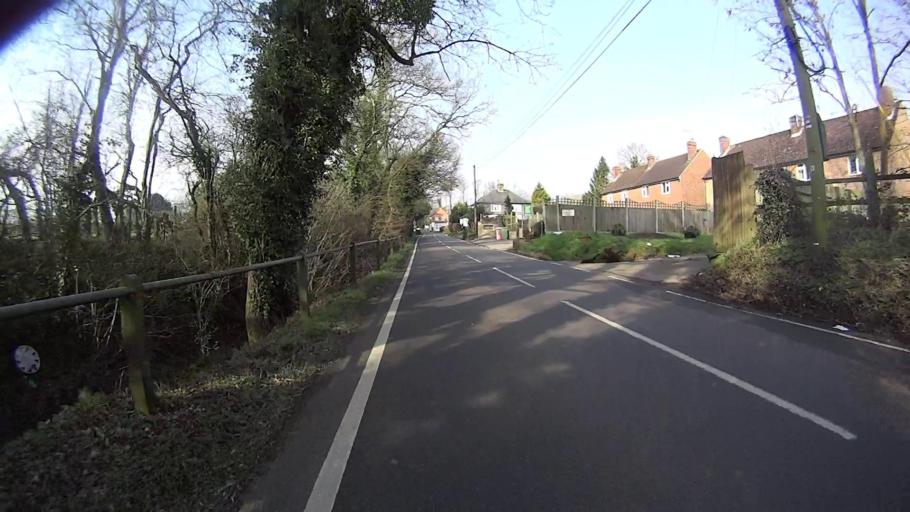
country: GB
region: England
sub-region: West Sussex
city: Copthorne
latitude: 51.1817
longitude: -0.0881
